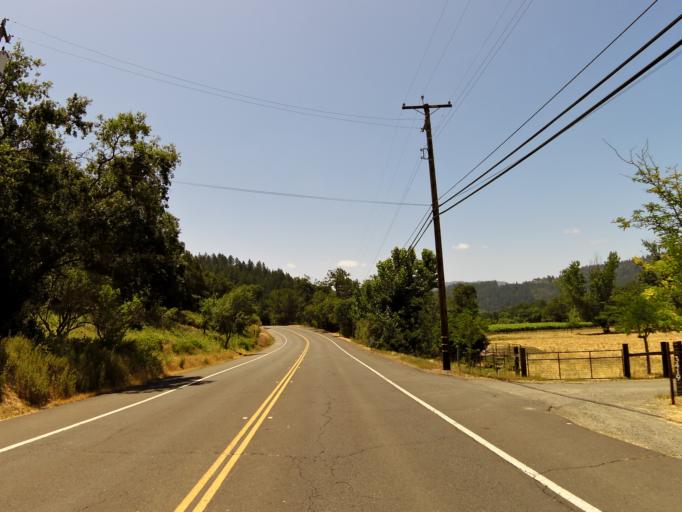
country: US
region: California
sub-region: Napa County
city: Deer Park
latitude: 38.5418
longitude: -122.4902
